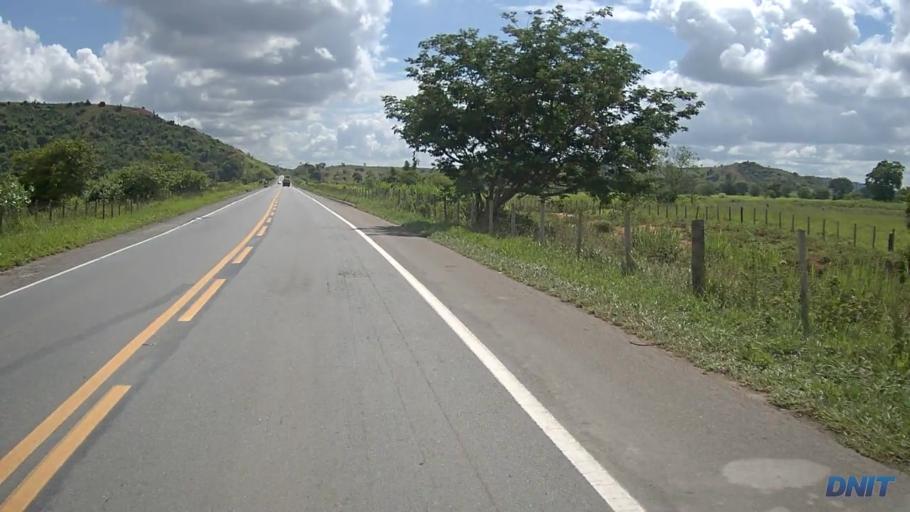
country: BR
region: Minas Gerais
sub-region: Governador Valadares
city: Governador Valadares
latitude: -19.0022
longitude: -42.1270
